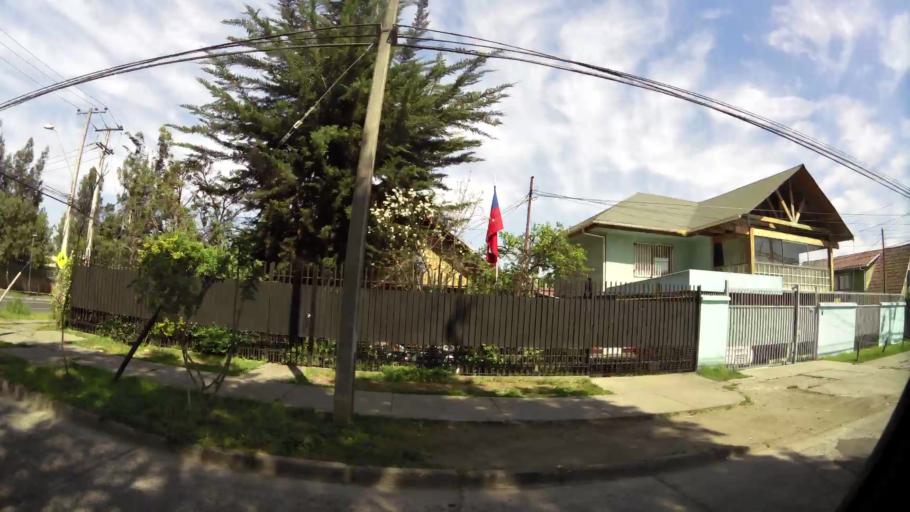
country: CL
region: Santiago Metropolitan
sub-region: Provincia de Talagante
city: Talagante
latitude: -33.6692
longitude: -70.9258
